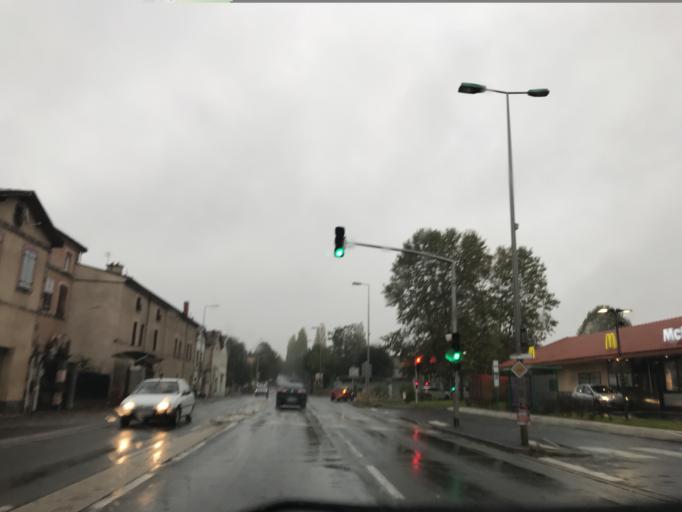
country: FR
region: Auvergne
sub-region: Departement du Puy-de-Dome
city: Vertaizon
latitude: 45.7860
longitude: 3.2856
